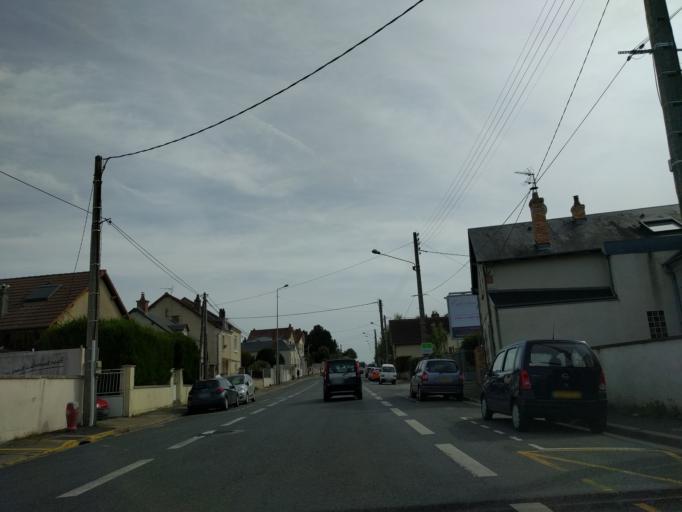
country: FR
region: Centre
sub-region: Departement du Cher
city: Bourges
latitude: 47.0647
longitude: 2.4199
